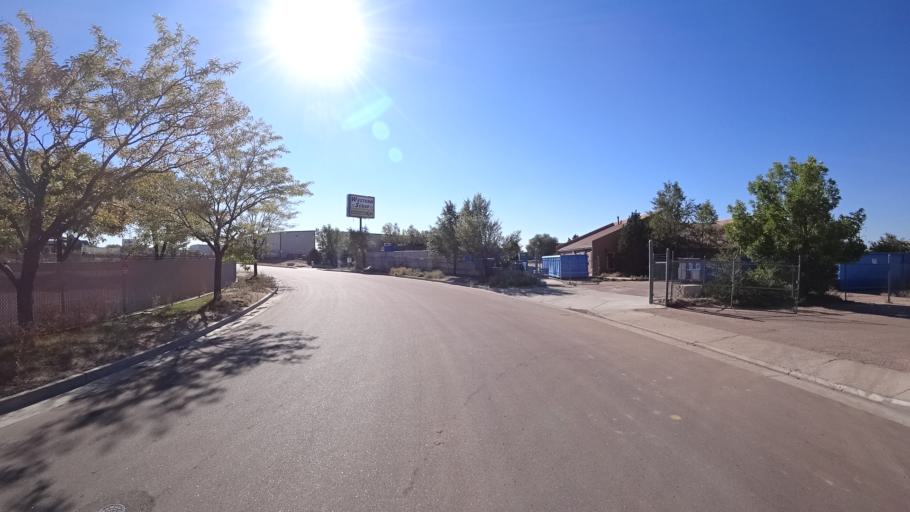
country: US
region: Colorado
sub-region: El Paso County
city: Stratmoor
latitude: 38.7863
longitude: -104.7698
